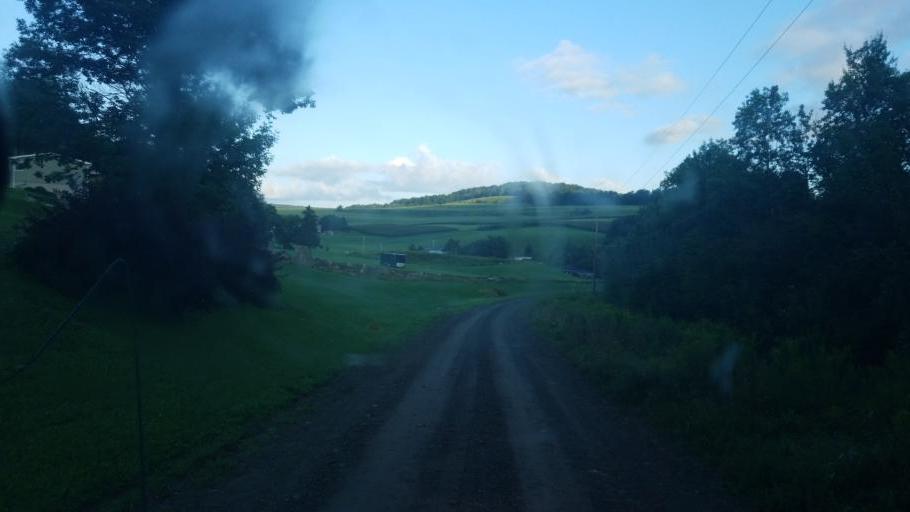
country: US
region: Pennsylvania
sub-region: Potter County
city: Galeton
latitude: 41.8791
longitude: -77.8117
